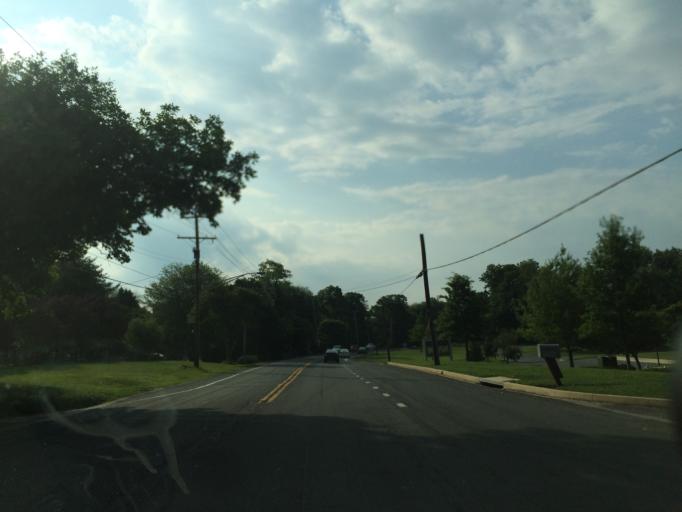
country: US
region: Maryland
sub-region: Montgomery County
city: Ashton-Sandy Spring
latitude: 39.1420
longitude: -76.9985
